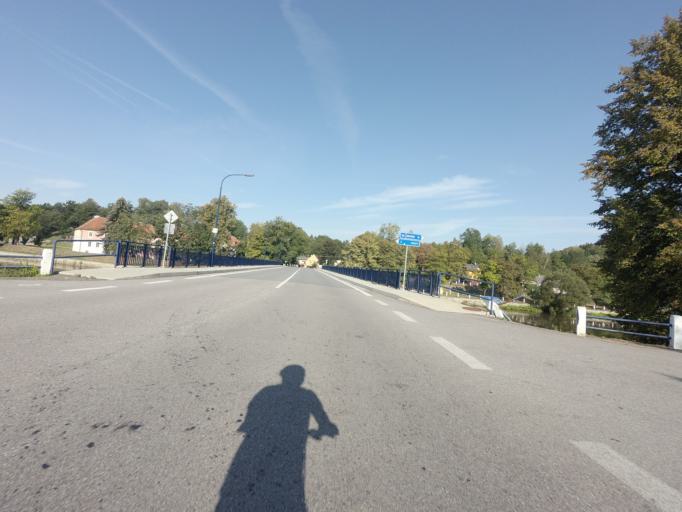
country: CZ
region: Jihocesky
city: Tyn nad Vltavou
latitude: 49.2527
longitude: 14.4209
